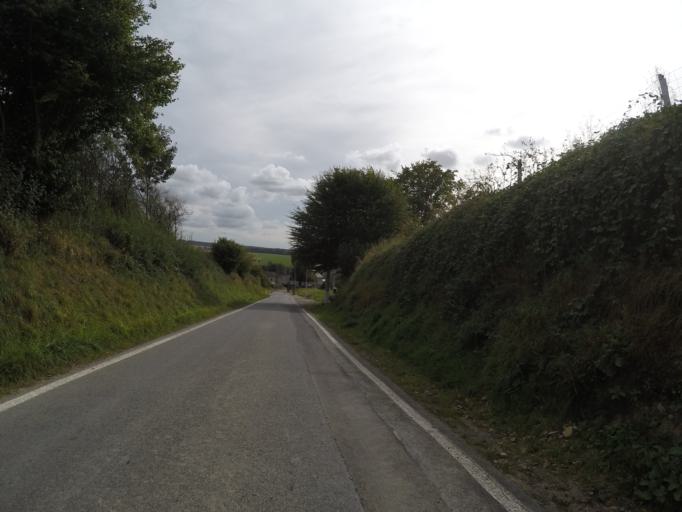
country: BE
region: Wallonia
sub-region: Province de Namur
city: Assesse
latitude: 50.3190
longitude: 4.9763
